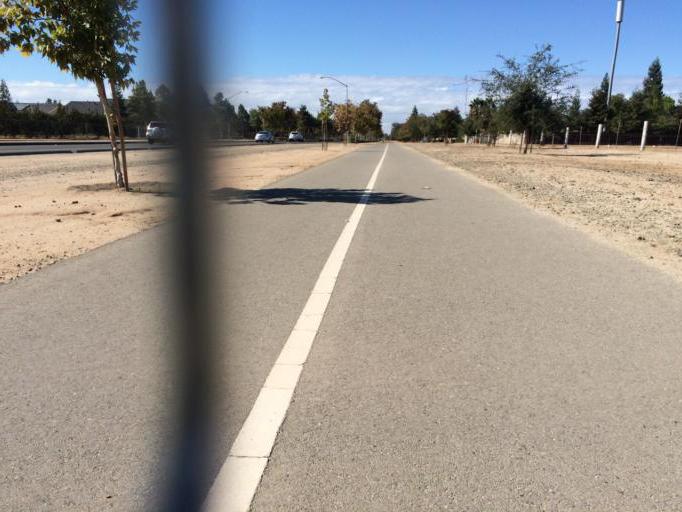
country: US
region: California
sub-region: Fresno County
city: Clovis
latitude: 36.8669
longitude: -119.7332
